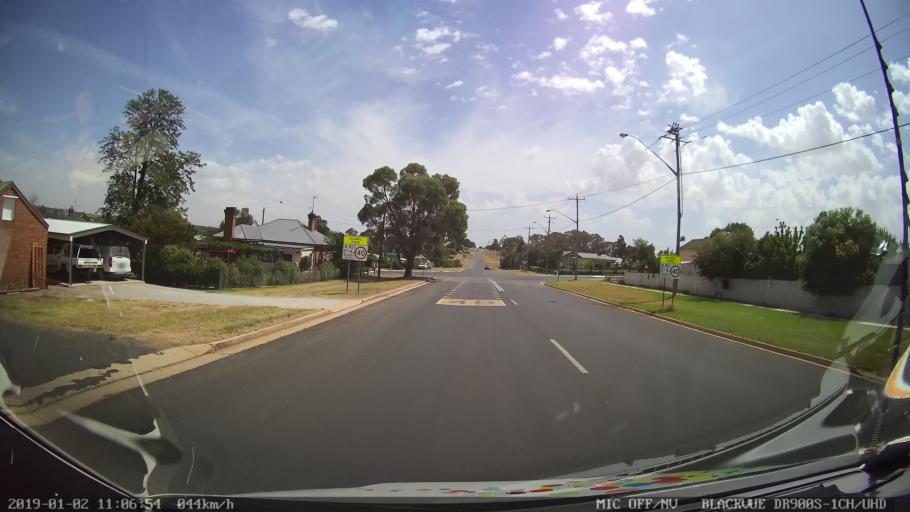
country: AU
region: New South Wales
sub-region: Young
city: Young
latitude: -34.5523
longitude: 148.3578
